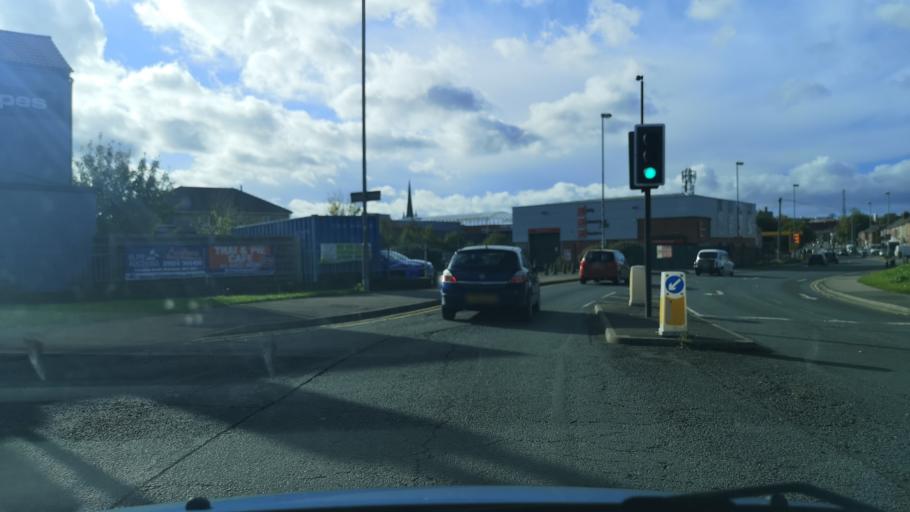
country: GB
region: England
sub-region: City and Borough of Wakefield
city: Wakefield
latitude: 53.6870
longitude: -1.4886
